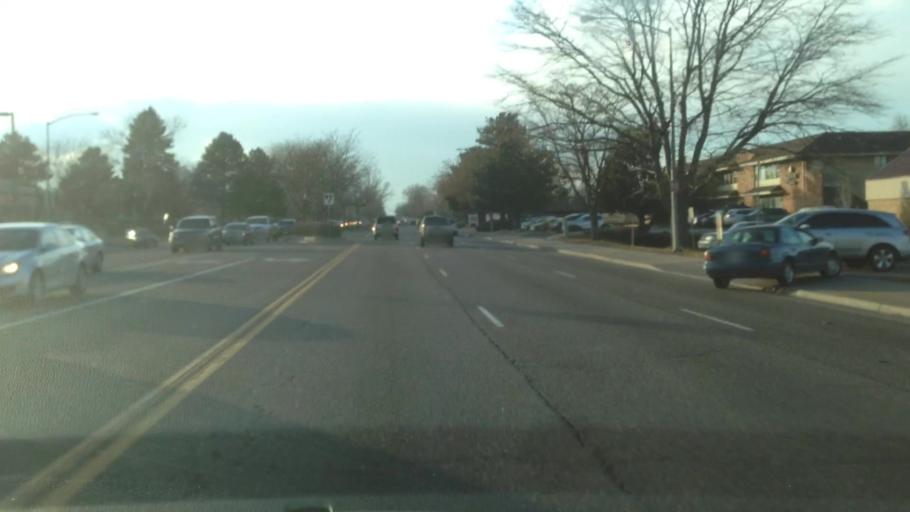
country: US
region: Colorado
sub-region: Adams County
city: Aurora
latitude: 39.6749
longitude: -104.8104
